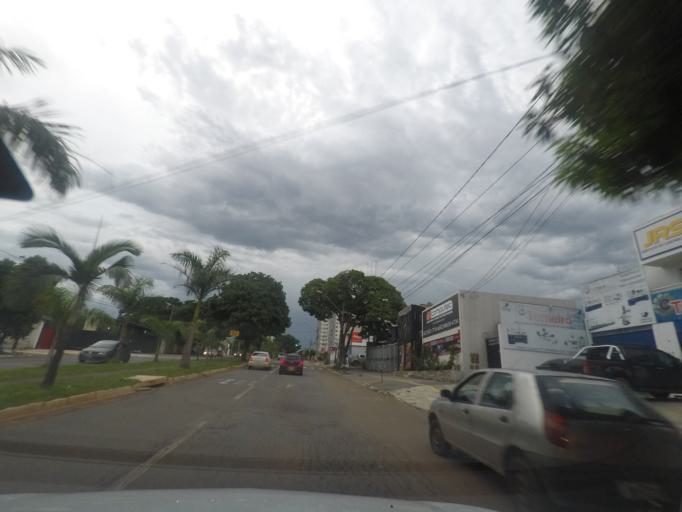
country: BR
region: Goias
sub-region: Goiania
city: Goiania
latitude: -16.7129
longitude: -49.2480
